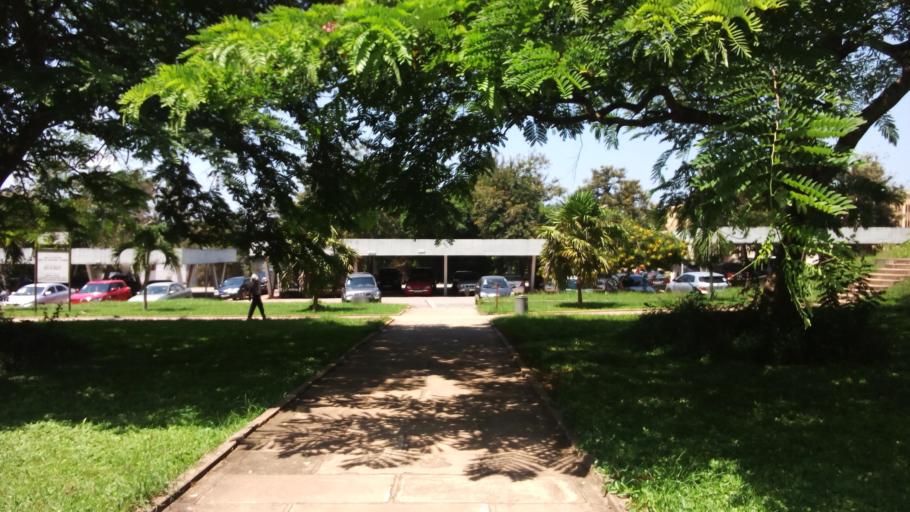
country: GH
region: Central
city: Cape Coast
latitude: 5.1178
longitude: -1.2924
